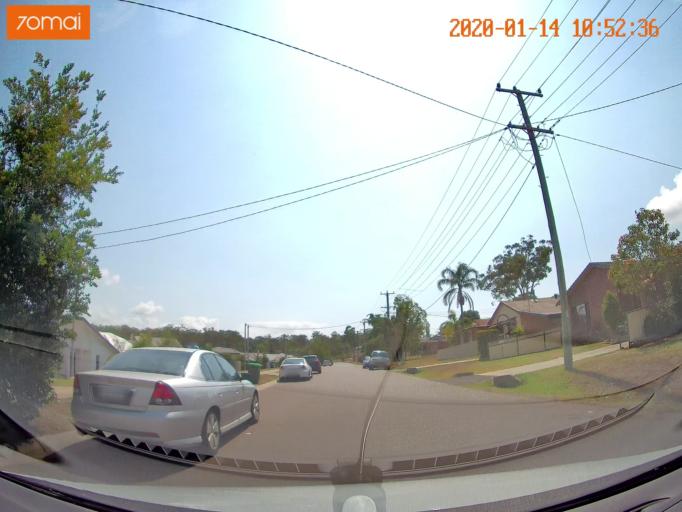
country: AU
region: New South Wales
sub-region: Lake Macquarie Shire
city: Dora Creek
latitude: -33.1004
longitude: 151.4832
